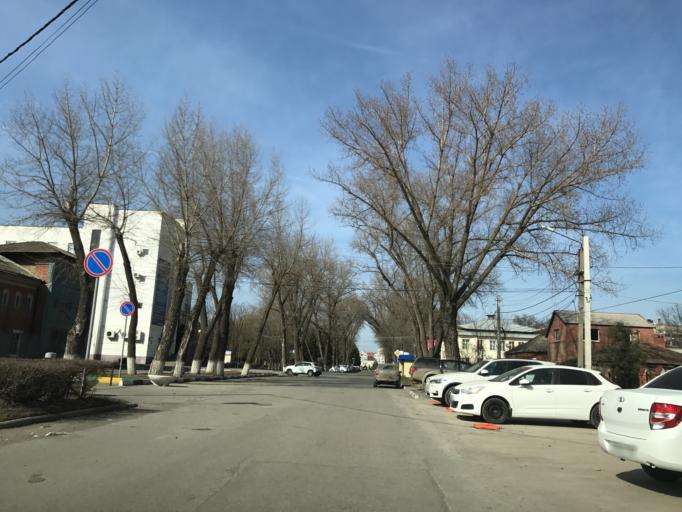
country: RU
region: Rostov
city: Bataysk
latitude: 47.1350
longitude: 39.7455
